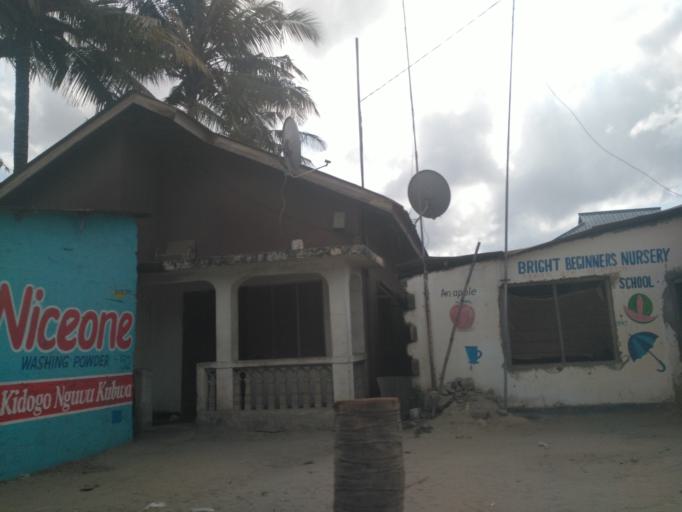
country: TZ
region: Dar es Salaam
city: Dar es Salaam
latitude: -6.9012
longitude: 39.2840
